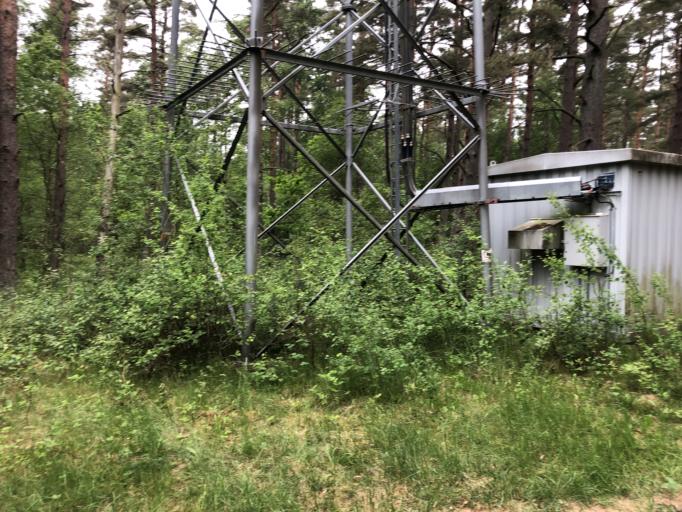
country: SE
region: Skane
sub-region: Lunds Kommun
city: Veberod
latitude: 55.6652
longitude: 13.5560
